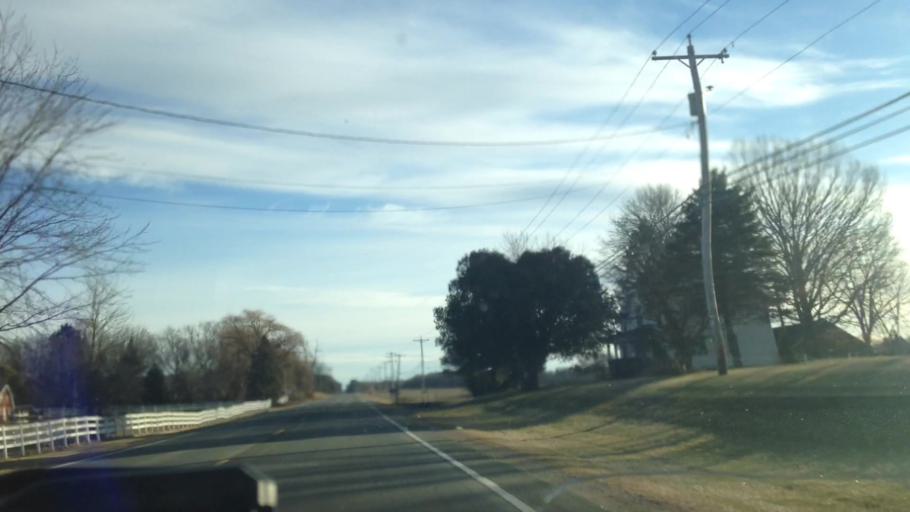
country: US
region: Wisconsin
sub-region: Washington County
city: Germantown
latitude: 43.2937
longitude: -88.0806
